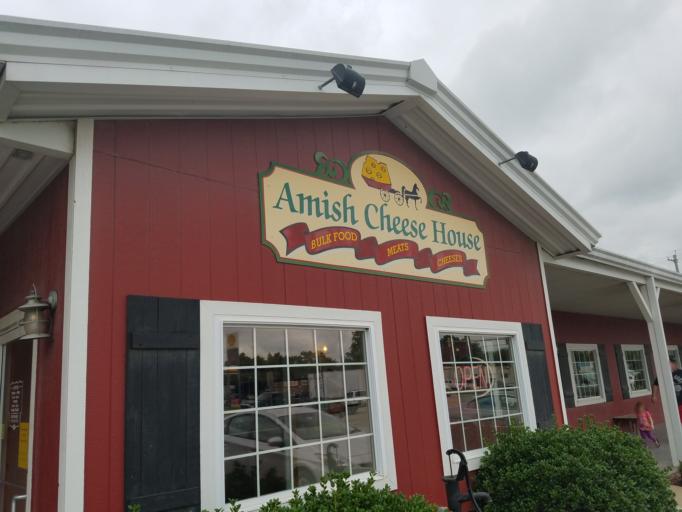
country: US
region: Oklahoma
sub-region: Mayes County
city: Chouteau
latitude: 36.1858
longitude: -95.3432
